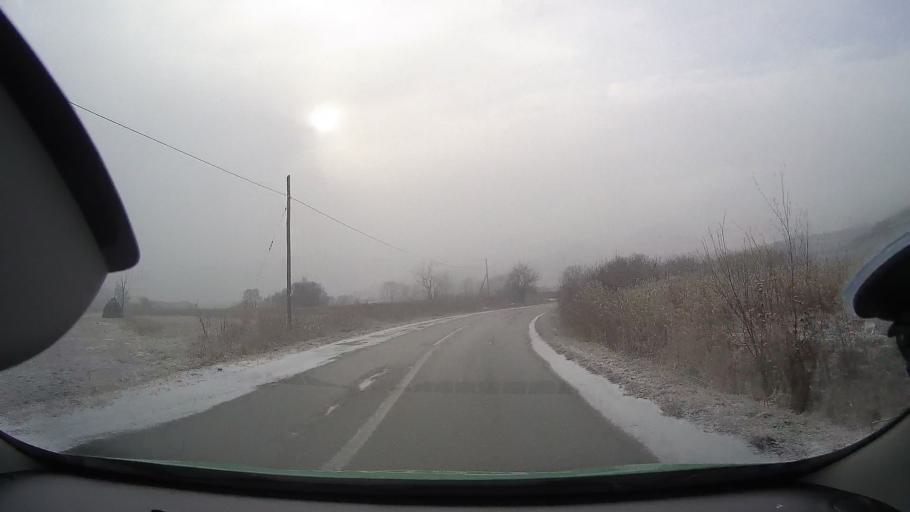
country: RO
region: Alba
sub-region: Comuna Rimetea
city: Rimetea
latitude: 46.4066
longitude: 23.5576
